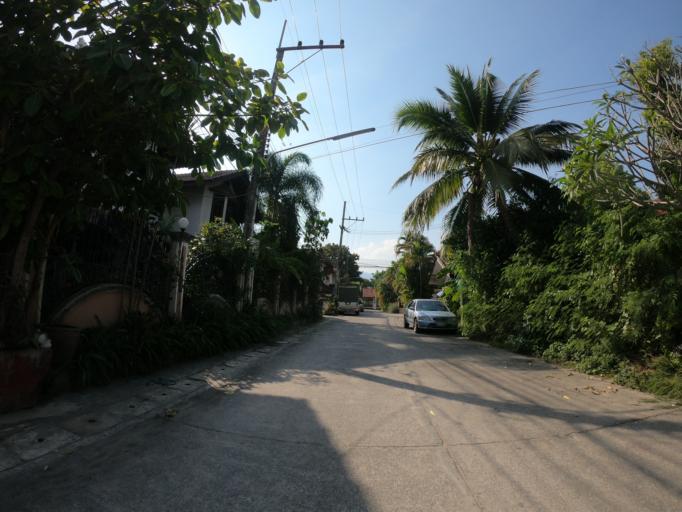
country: TH
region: Chiang Mai
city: Chiang Mai
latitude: 18.8232
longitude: 99.0015
